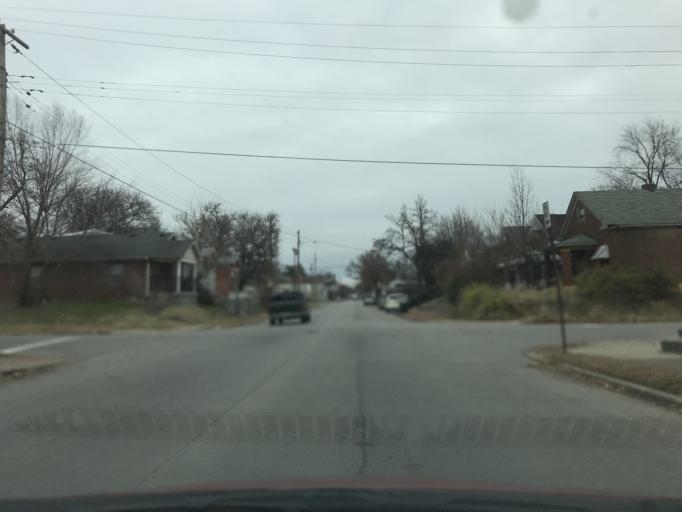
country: US
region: Kentucky
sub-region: Jefferson County
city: Louisville
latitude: 38.2554
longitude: -85.7854
